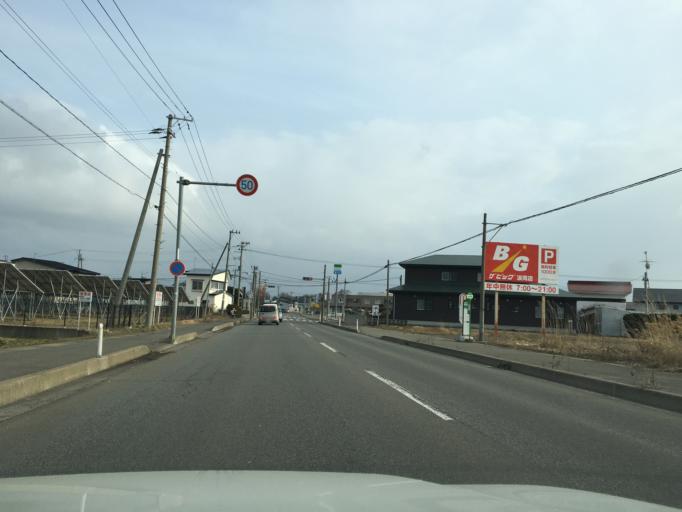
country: JP
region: Aomori
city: Namioka
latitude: 40.7184
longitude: 140.5893
